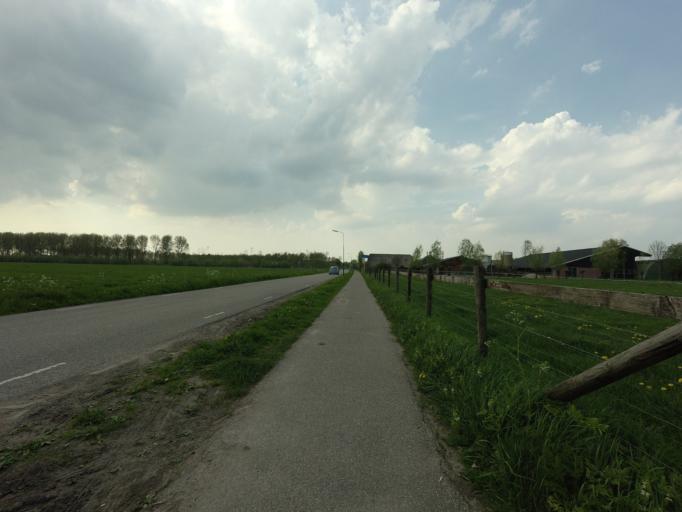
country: NL
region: Utrecht
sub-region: Gemeente Houten
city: Houten
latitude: 51.9950
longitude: 5.1554
